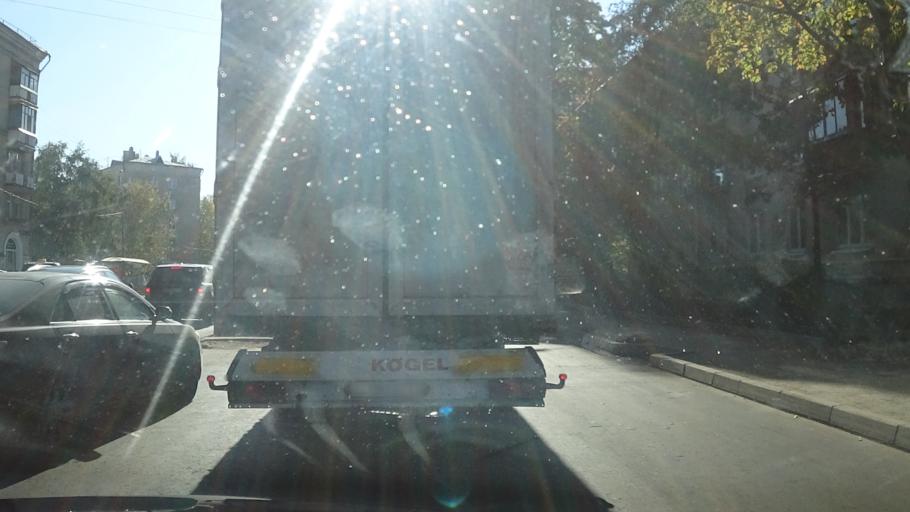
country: RU
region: Moskovskaya
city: Bol'shaya Setun'
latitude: 55.7359
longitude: 37.4082
